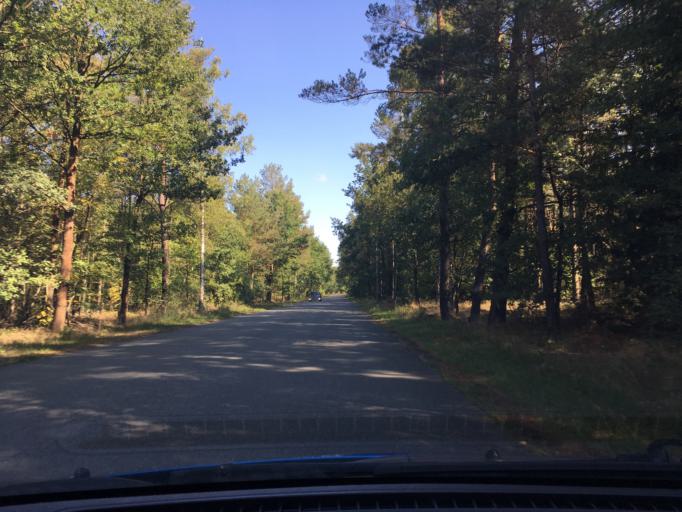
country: DE
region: Lower Saxony
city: Munster
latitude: 52.9606
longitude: 10.1315
